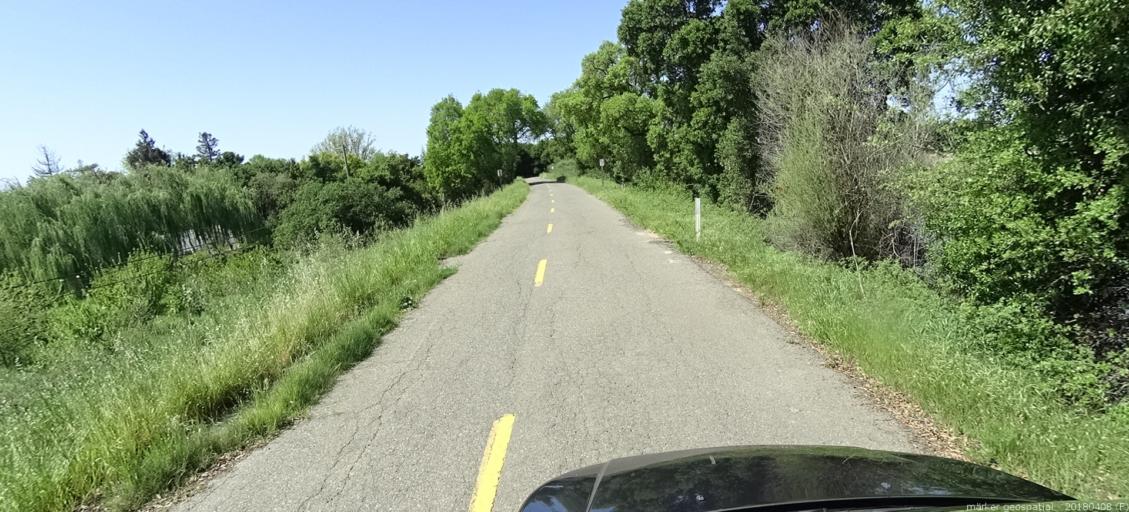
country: US
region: California
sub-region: Sacramento County
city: Walnut Grove
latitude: 38.2271
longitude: -121.5105
